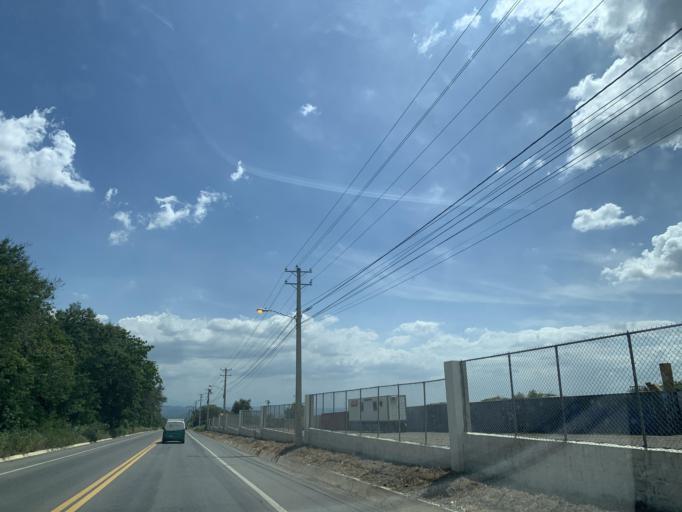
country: DO
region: Santiago
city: Villa Bisono
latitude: 19.5787
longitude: -70.8473
